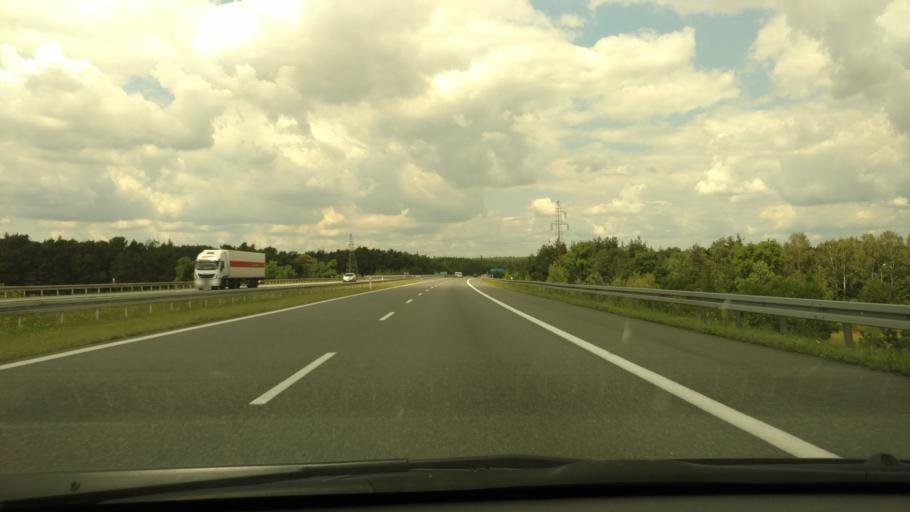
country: PL
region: Silesian Voivodeship
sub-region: Powiat bierunsko-ledzinski
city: Imielin
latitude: 50.1797
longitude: 19.1989
